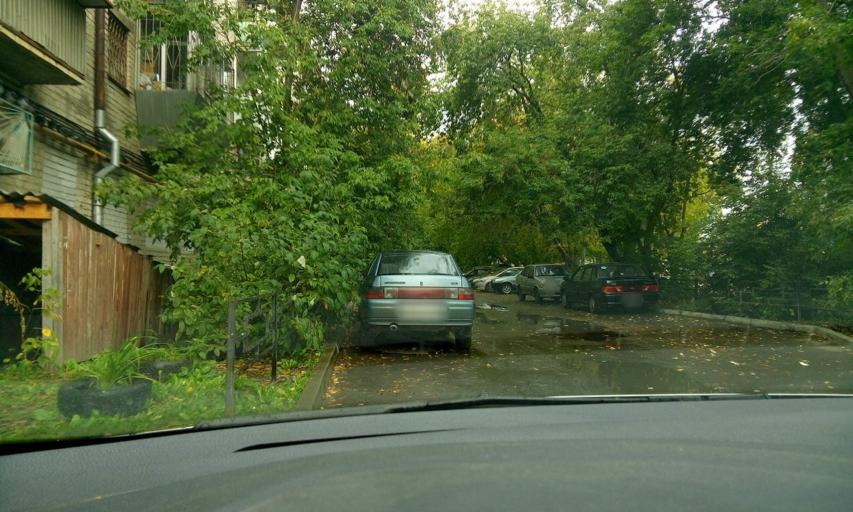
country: RU
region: Sverdlovsk
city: Yekaterinburg
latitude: 56.8048
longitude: 60.6267
